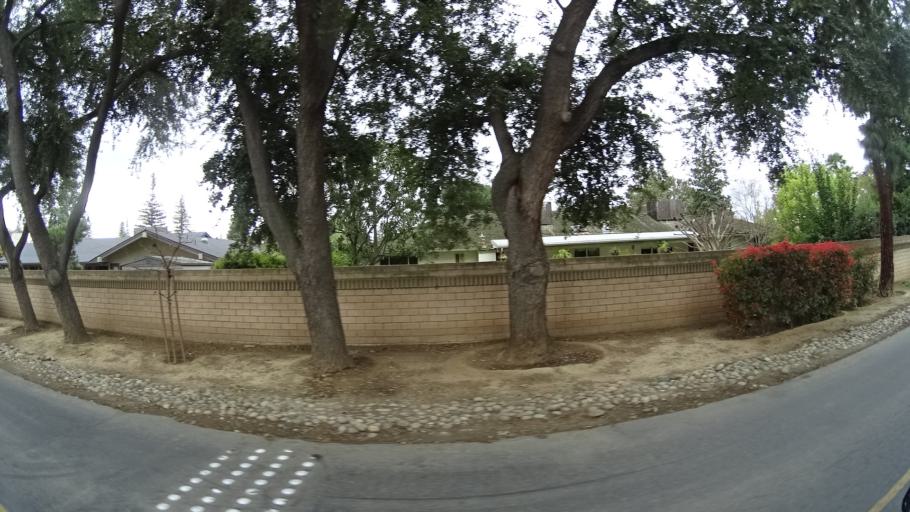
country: US
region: California
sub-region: Fresno County
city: Fresno
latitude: 36.8477
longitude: -119.8486
